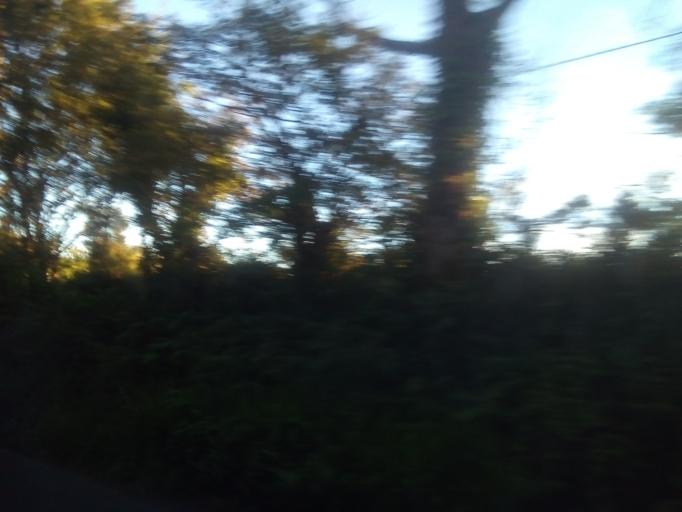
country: IE
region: Leinster
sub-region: Loch Garman
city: Loch Garman
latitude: 52.2813
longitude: -6.4953
